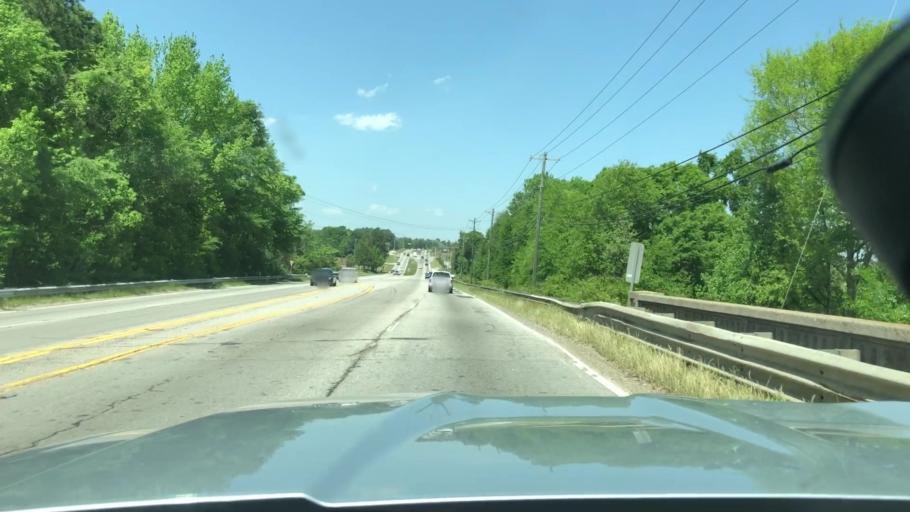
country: US
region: South Carolina
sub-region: Lexington County
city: Pineridge
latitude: 33.9092
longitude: -81.0671
